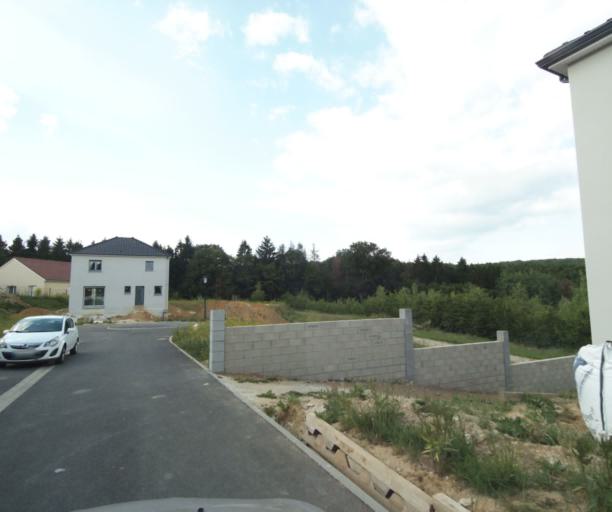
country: FR
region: Champagne-Ardenne
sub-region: Departement des Ardennes
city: Montcy-Notre-Dame
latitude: 49.7942
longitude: 4.7265
